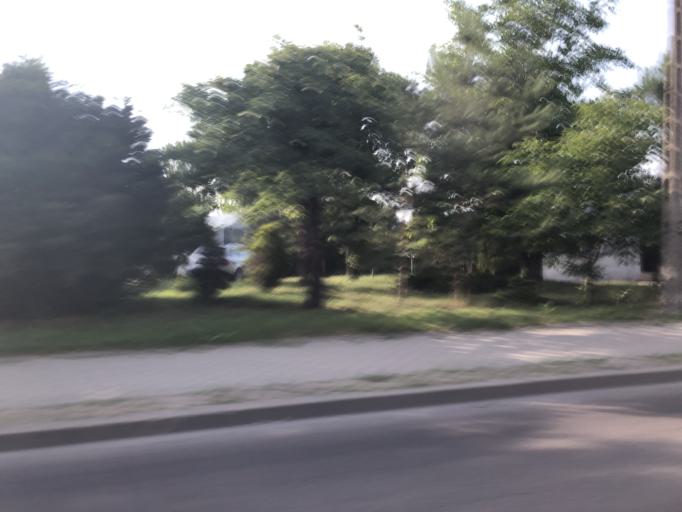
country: PL
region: Podlasie
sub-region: Lomza
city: Lomza
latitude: 53.1680
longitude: 22.0427
